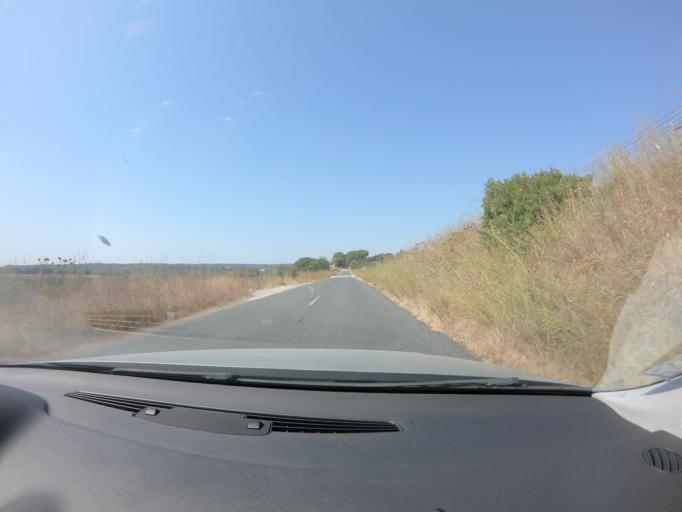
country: PT
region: Setubal
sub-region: Alcacer do Sal
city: Alcacer do Sal
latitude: 38.2735
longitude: -8.3689
